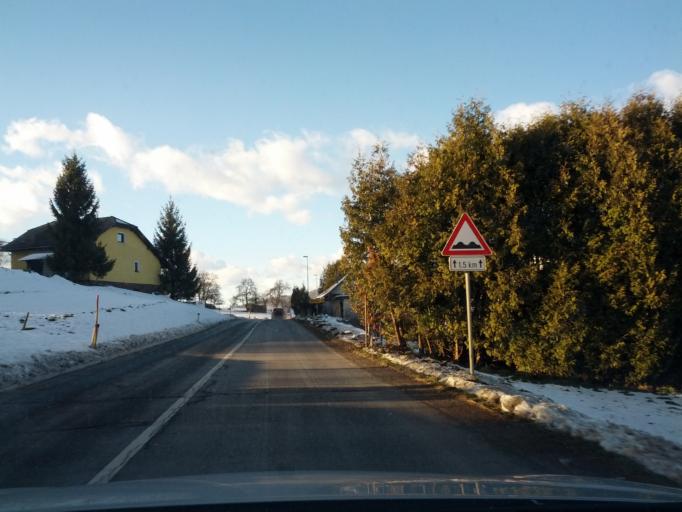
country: SI
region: Moravce
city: Moravce
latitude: 46.1296
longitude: 14.7501
